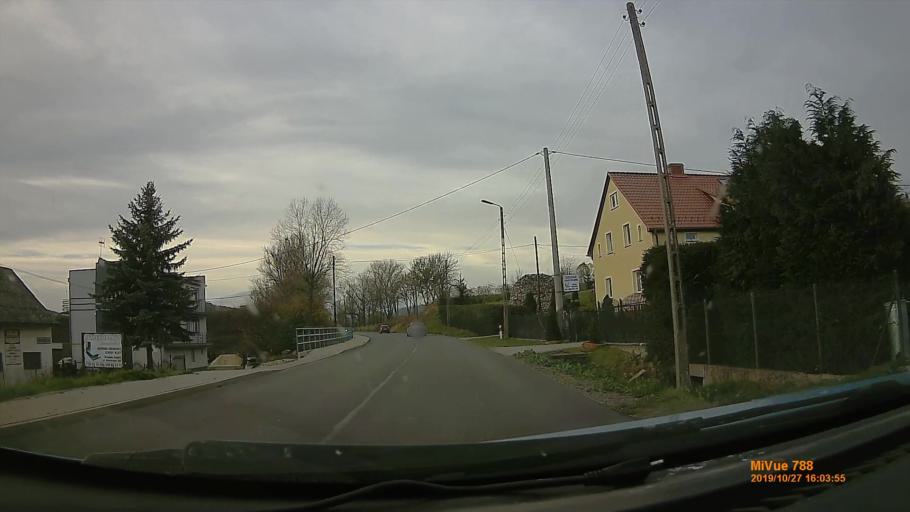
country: PL
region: Lower Silesian Voivodeship
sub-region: Powiat klodzki
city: Nowa Ruda
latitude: 50.5233
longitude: 16.4934
